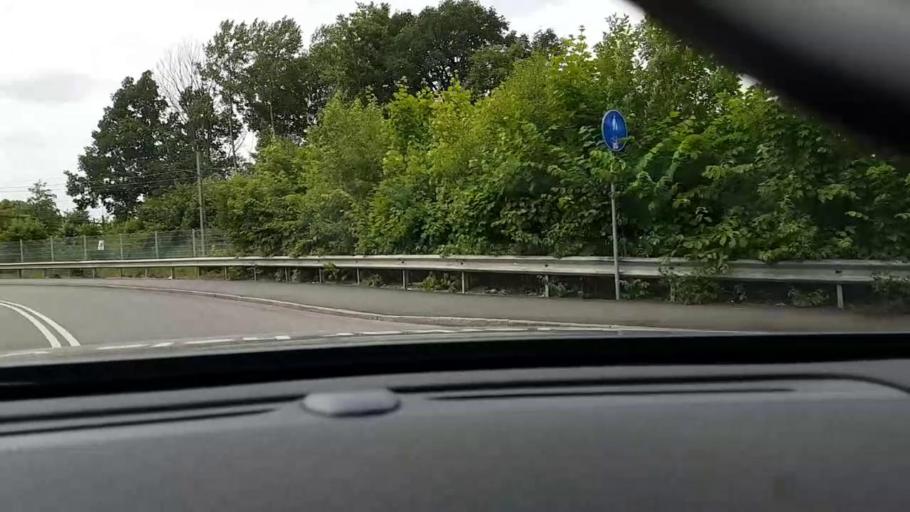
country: SE
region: Skane
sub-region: Hassleholms Kommun
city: Hassleholm
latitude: 56.1611
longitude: 13.7668
